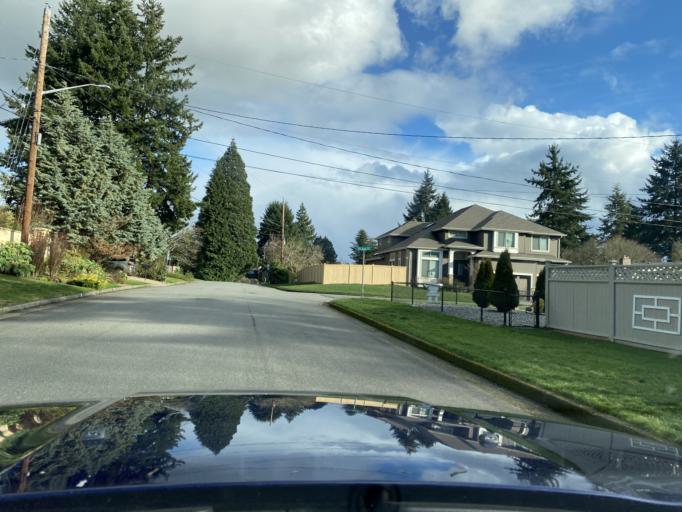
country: US
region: Washington
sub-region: King County
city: Bellevue
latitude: 47.6063
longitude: -122.1941
